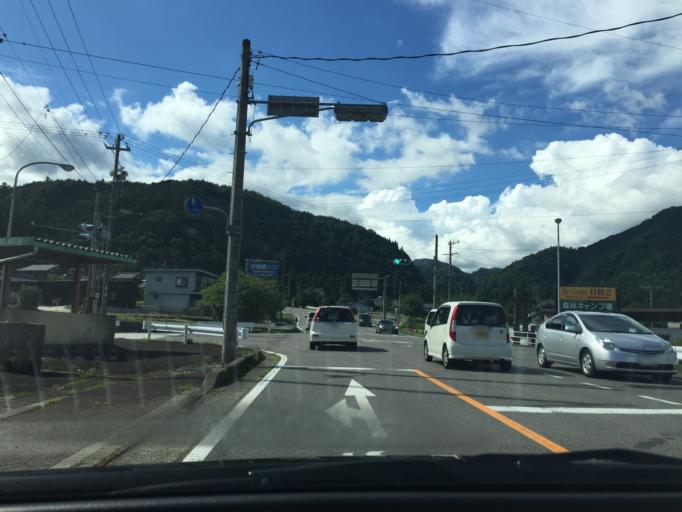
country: JP
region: Gifu
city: Nakatsugawa
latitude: 35.6761
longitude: 137.4157
